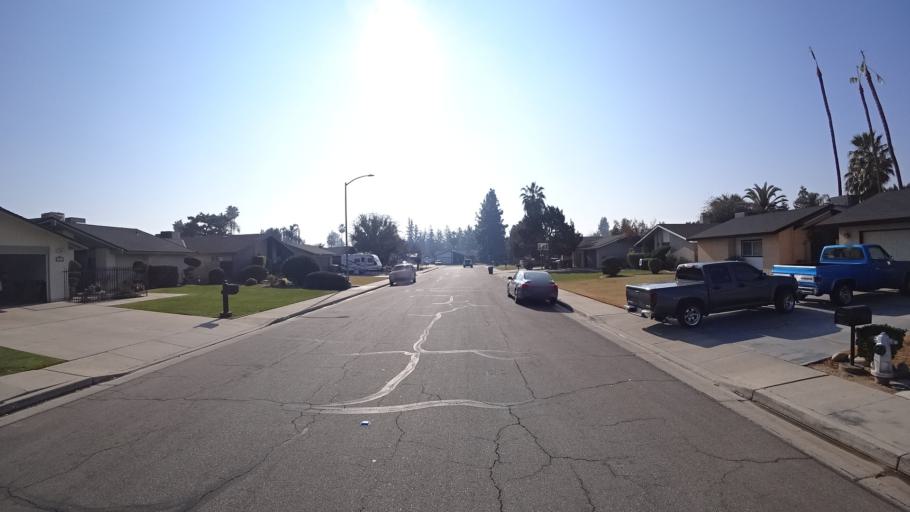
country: US
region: California
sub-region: Kern County
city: Greenacres
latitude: 35.3581
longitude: -119.0769
